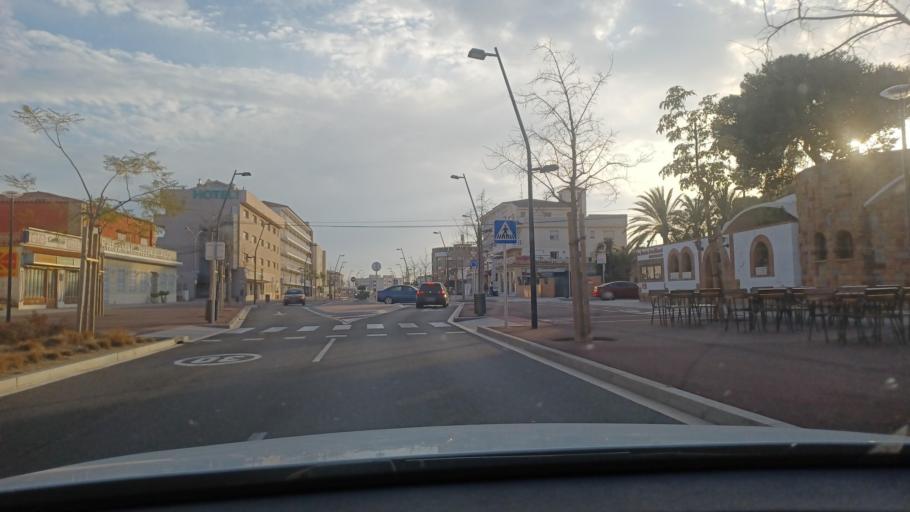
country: ES
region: Catalonia
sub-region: Provincia de Tarragona
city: Colldejou
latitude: 41.0049
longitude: 0.9346
